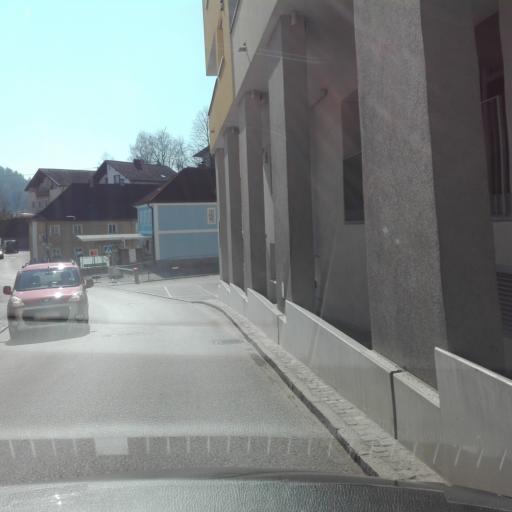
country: AT
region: Upper Austria
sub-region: Politischer Bezirk Perg
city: Perg
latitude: 48.3492
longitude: 14.6694
